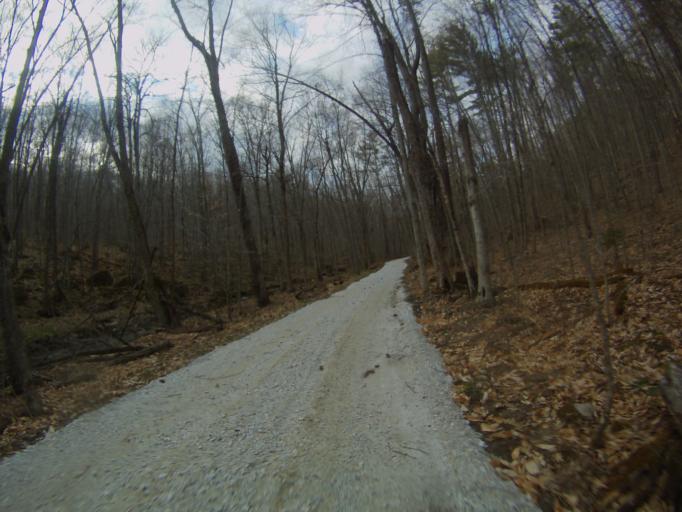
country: US
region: Vermont
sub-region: Rutland County
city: Brandon
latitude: 43.8435
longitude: -73.0424
